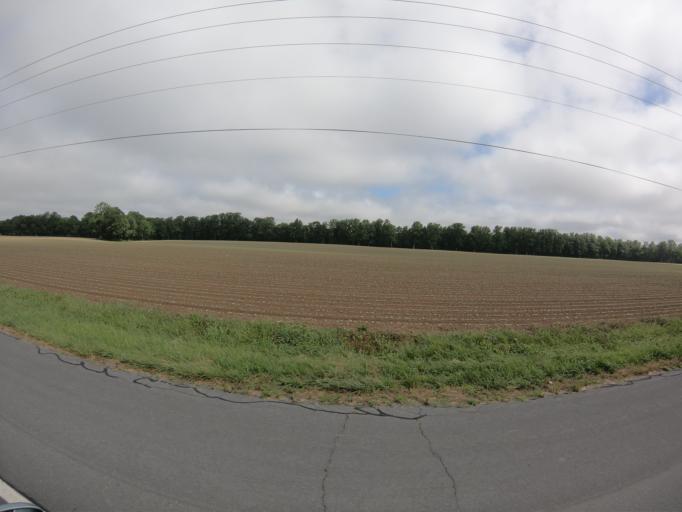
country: US
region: Delaware
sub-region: Kent County
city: Riverview
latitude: 39.0056
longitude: -75.5331
